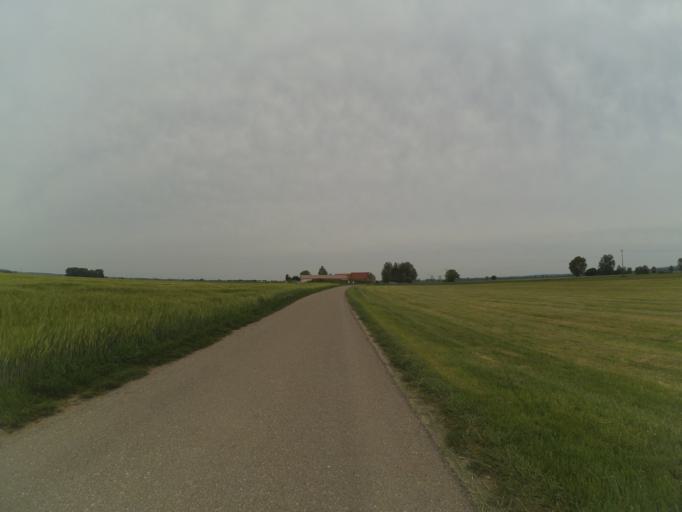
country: DE
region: Baden-Wuerttemberg
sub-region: Regierungsbezirk Stuttgart
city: Sontheim an der Brenz
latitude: 48.5204
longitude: 10.2801
